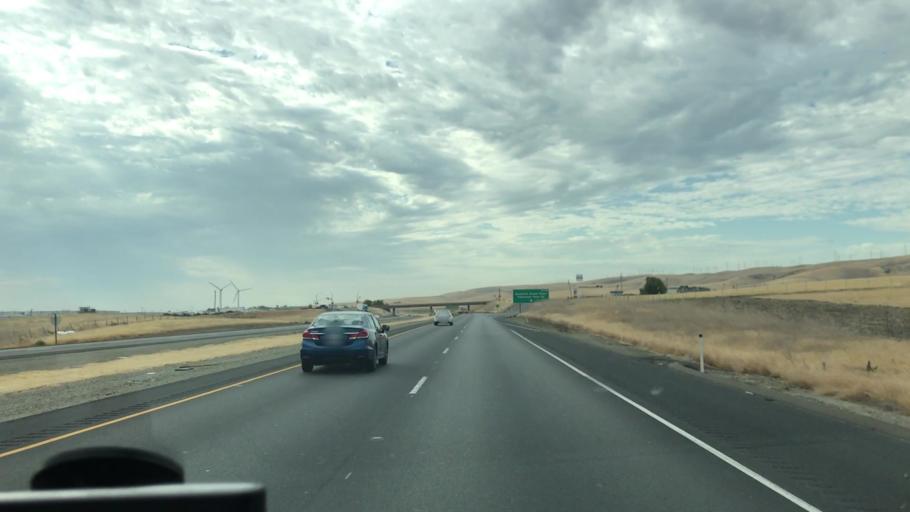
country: US
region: California
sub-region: San Joaquin County
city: Mountain House
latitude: 37.7235
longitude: -121.5400
